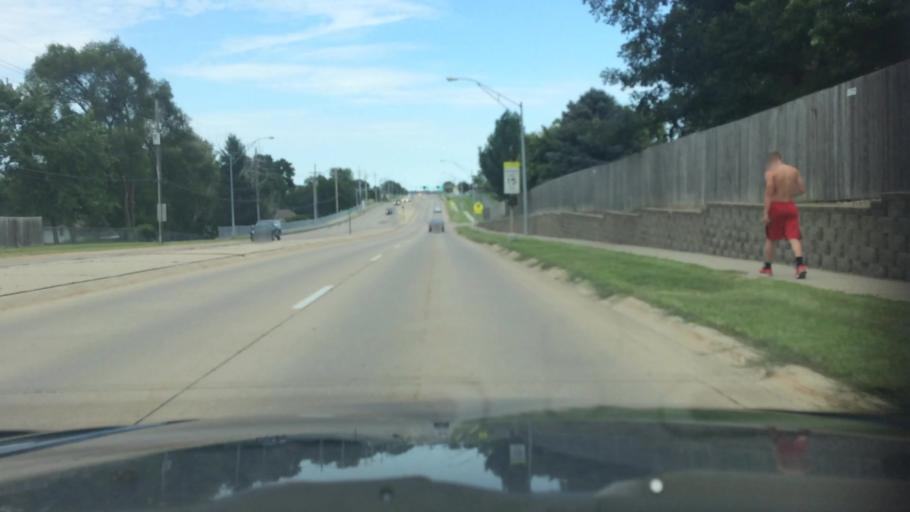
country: US
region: Nebraska
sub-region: Sarpy County
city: La Vista
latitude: 41.1762
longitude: -96.0352
